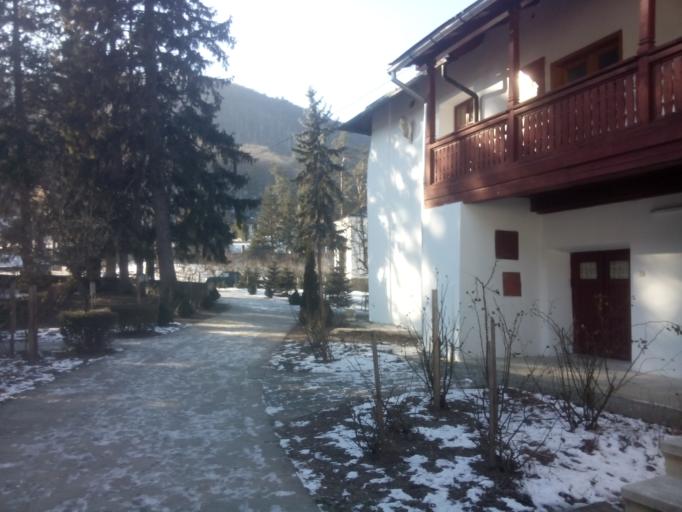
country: RO
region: Valcea
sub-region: Oras Calimanesti
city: Calimanesti
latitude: 45.2719
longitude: 24.3158
